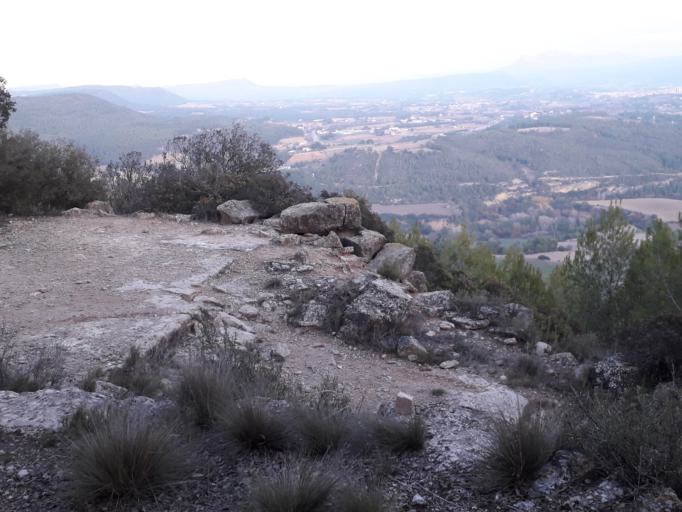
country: ES
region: Catalonia
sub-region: Provincia de Barcelona
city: Jorba
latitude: 41.5914
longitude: 1.5377
